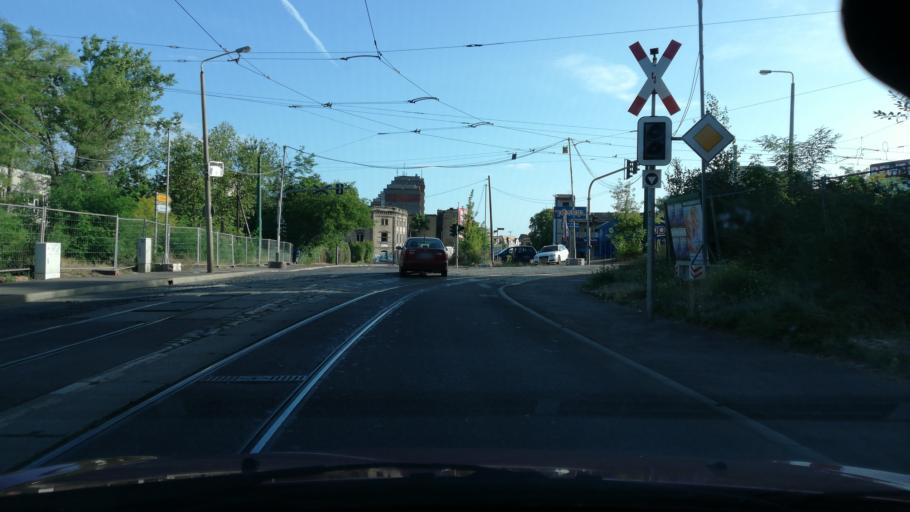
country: DE
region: Saxony-Anhalt
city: Halle Neustadt
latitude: 51.4735
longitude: 11.9602
